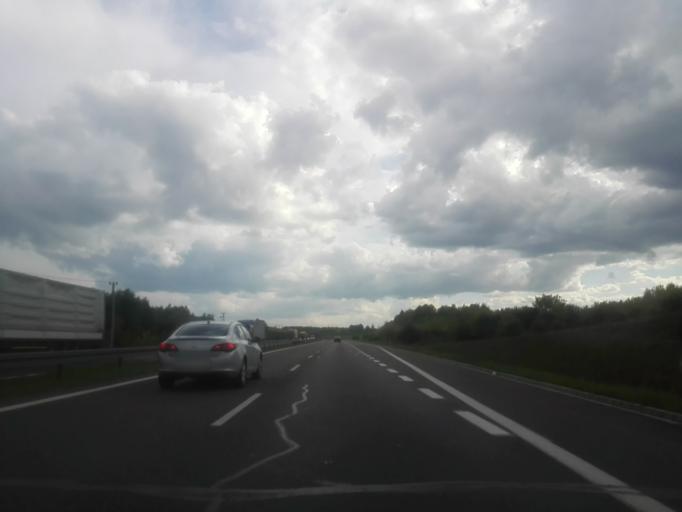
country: PL
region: Masovian Voivodeship
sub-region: Powiat ostrowski
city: Ostrow Mazowiecka
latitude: 52.8052
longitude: 21.8739
